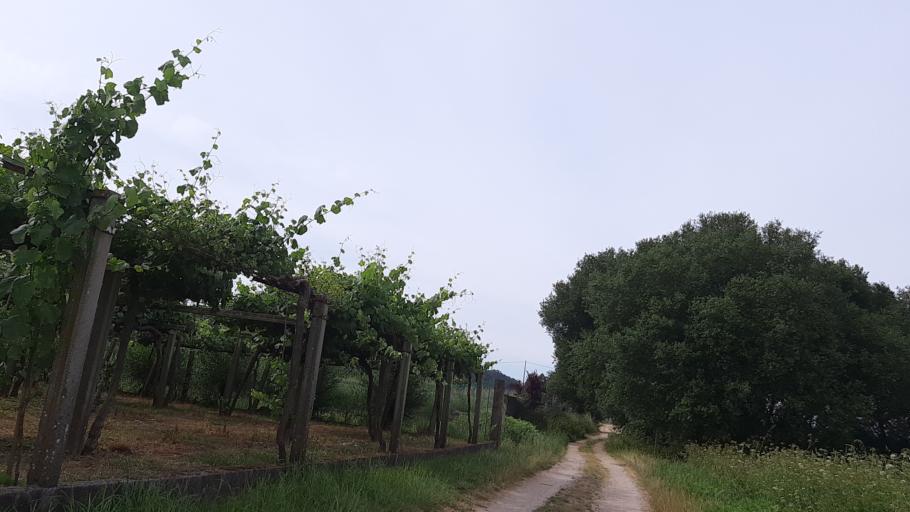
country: ES
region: Galicia
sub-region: Provincia de Pontevedra
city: O Rosal
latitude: 41.9275
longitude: -8.8294
